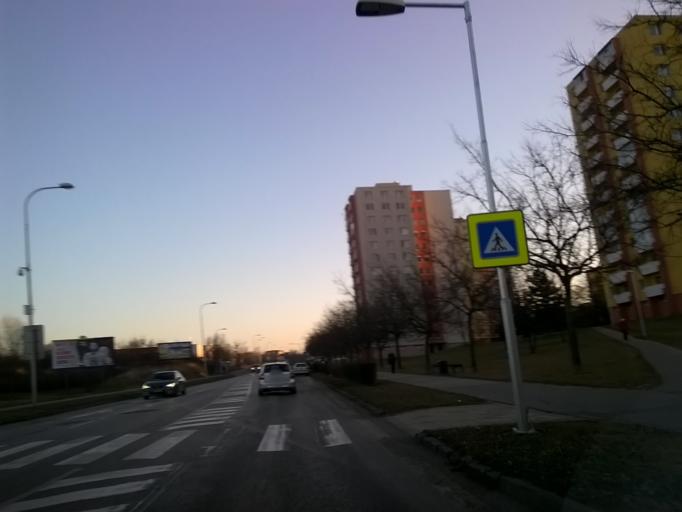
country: SK
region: Nitriansky
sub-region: Okres Nitra
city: Nitra
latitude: 48.3008
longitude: 18.0643
